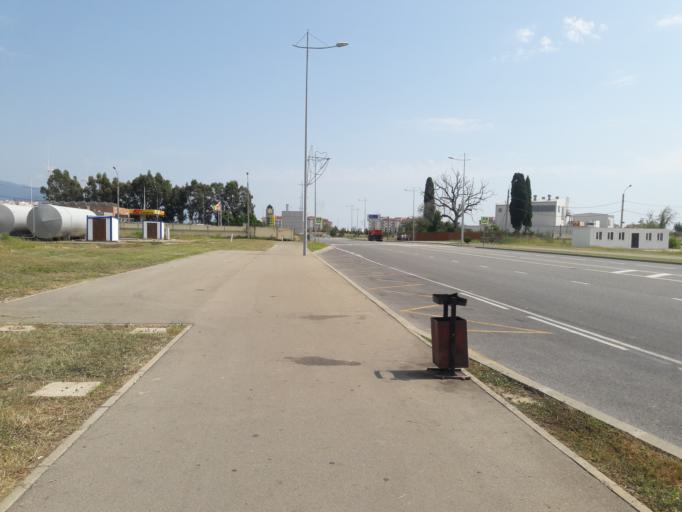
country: RU
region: Krasnodarskiy
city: Vysokoye
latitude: 43.3968
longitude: 39.9869
